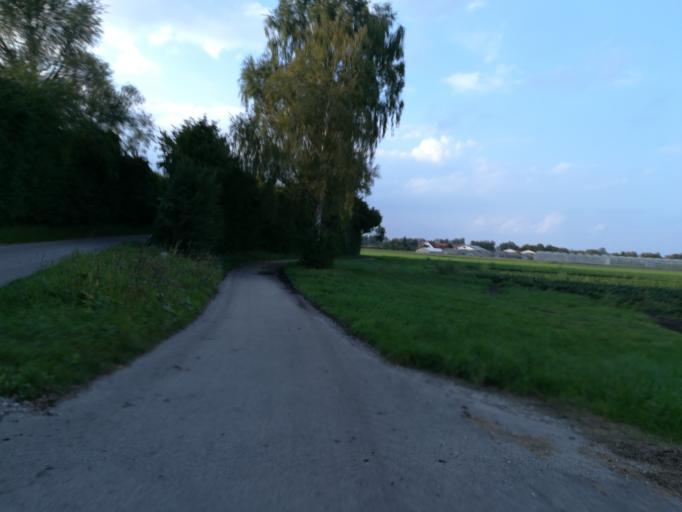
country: DE
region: Bavaria
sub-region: Upper Bavaria
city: Karlsfeld
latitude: 48.2490
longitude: 11.4752
